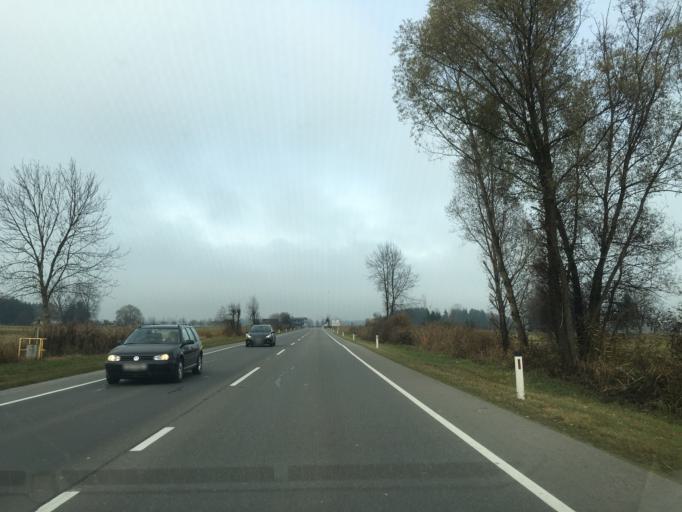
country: CH
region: Saint Gallen
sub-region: Wahlkreis Rheintal
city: Diepoldsau
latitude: 47.3942
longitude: 9.6810
